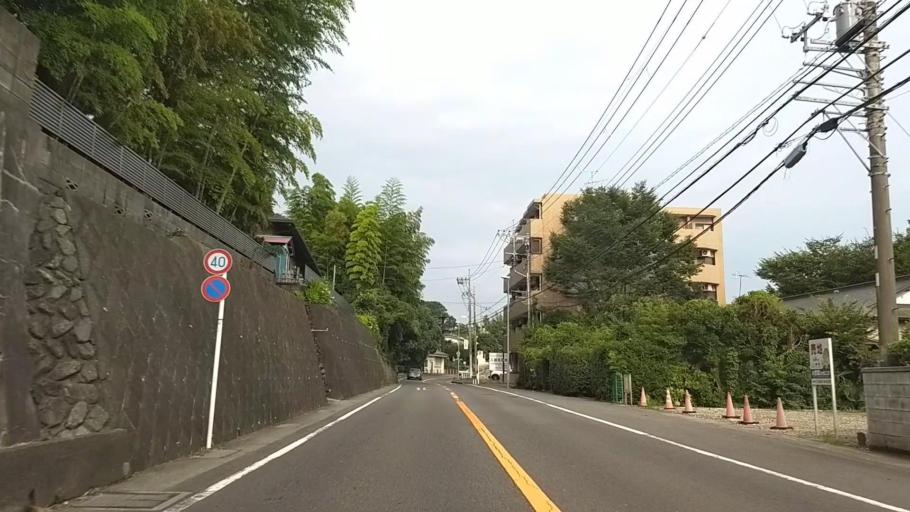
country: JP
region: Kanagawa
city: Oiso
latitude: 35.3284
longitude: 139.3128
